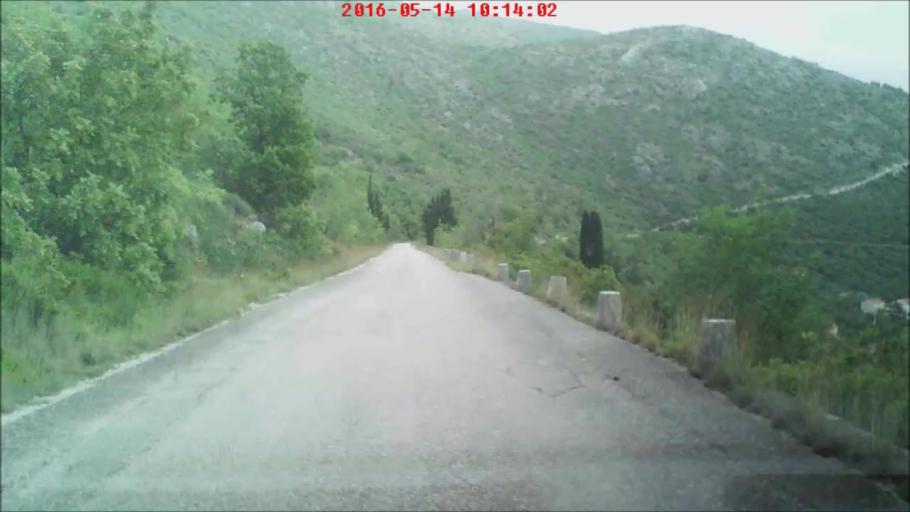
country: HR
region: Dubrovacko-Neretvanska
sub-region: Grad Dubrovnik
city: Mokosica
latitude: 42.7343
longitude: 17.9562
